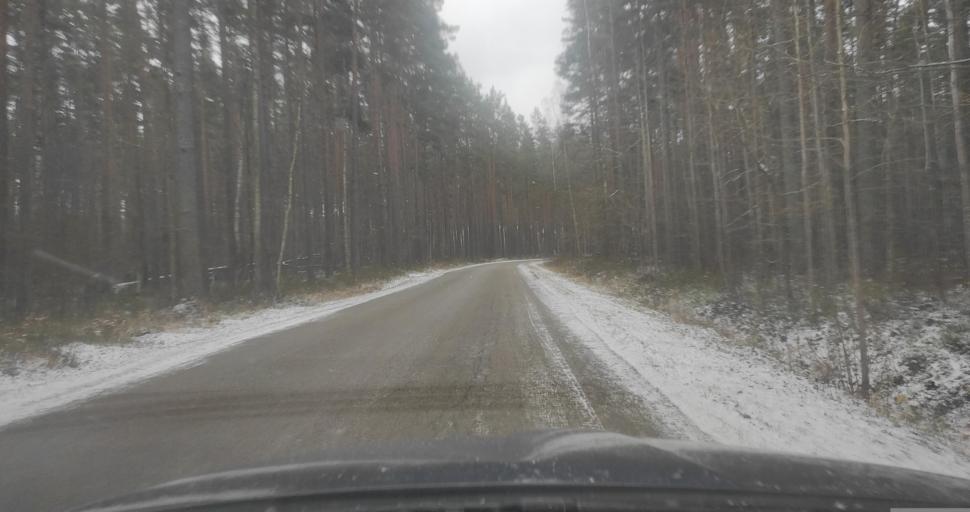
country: LV
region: Jurmala
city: Jurmala
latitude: 56.9157
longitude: 23.8199
